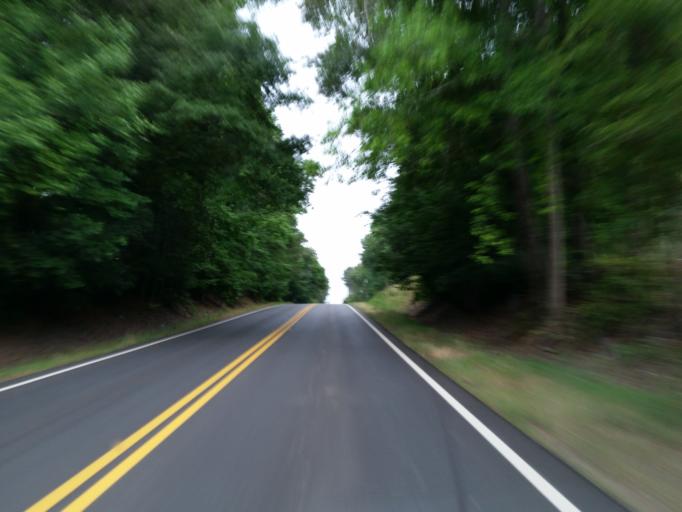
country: US
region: Georgia
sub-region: Dooly County
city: Unadilla
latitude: 32.3013
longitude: -83.7613
